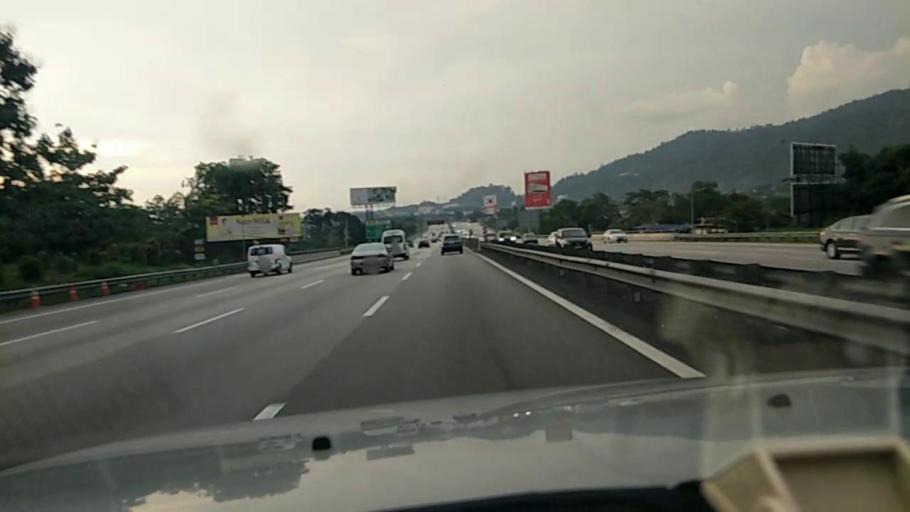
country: MY
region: Selangor
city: Kuang
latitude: 3.2147
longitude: 101.5814
